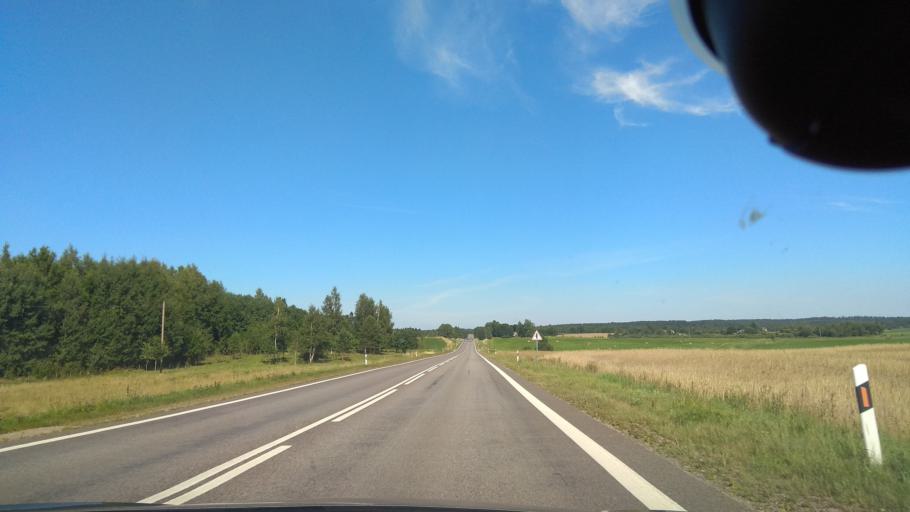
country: LT
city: Seda
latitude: 55.9832
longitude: 22.0350
